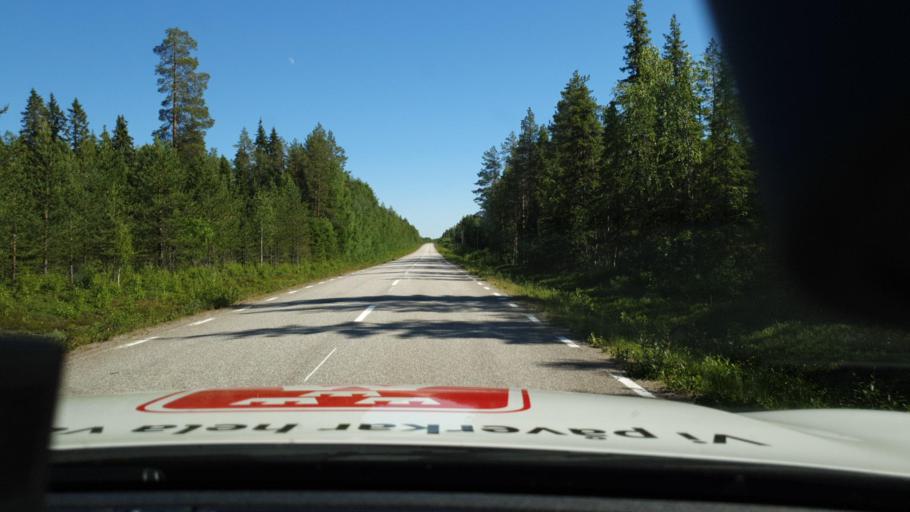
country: SE
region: Norrbotten
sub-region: Lulea Kommun
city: Ranea
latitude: 65.9860
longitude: 22.3517
